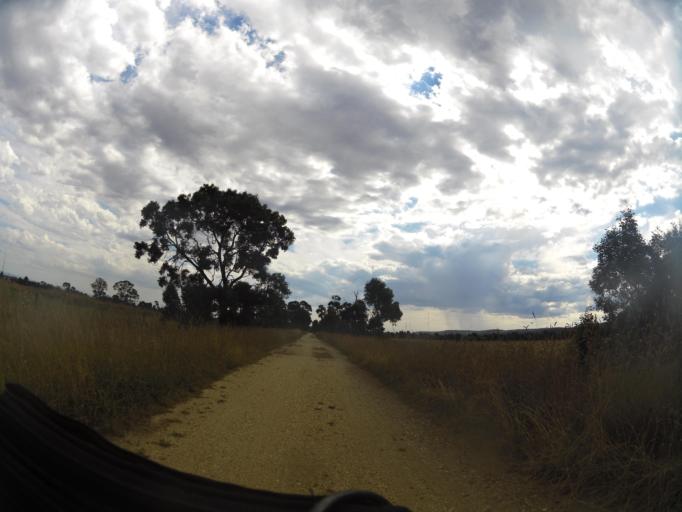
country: AU
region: Victoria
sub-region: Wellington
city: Heyfield
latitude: -38.0461
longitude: 146.6377
